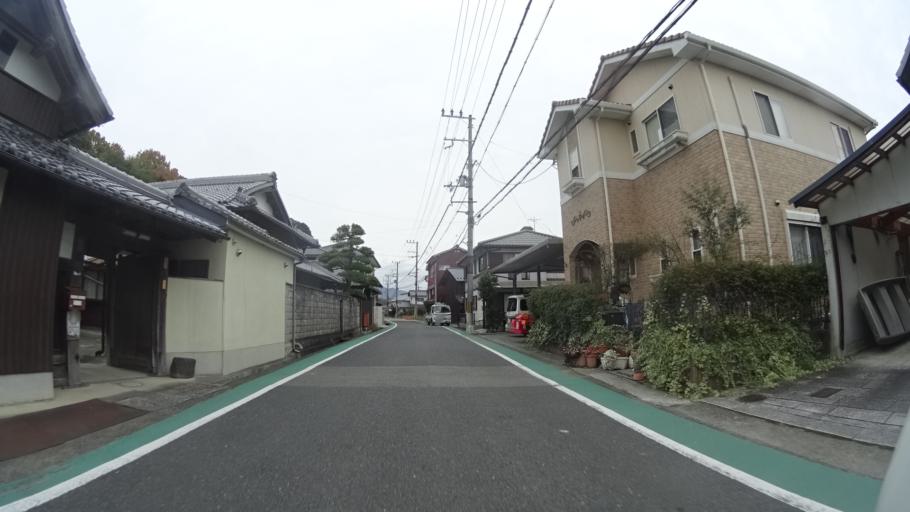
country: JP
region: Kyoto
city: Kameoka
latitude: 35.0585
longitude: 135.5450
